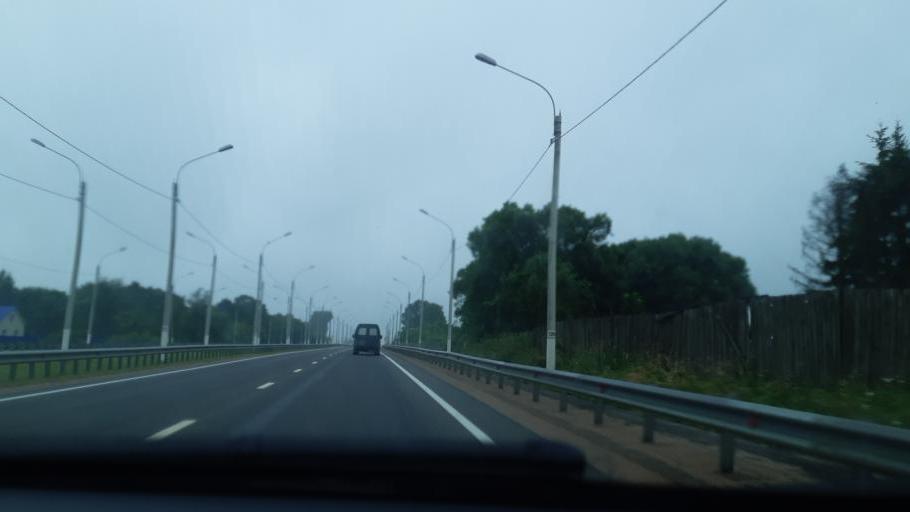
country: RU
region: Smolensk
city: Talashkino
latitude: 54.6389
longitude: 32.1790
